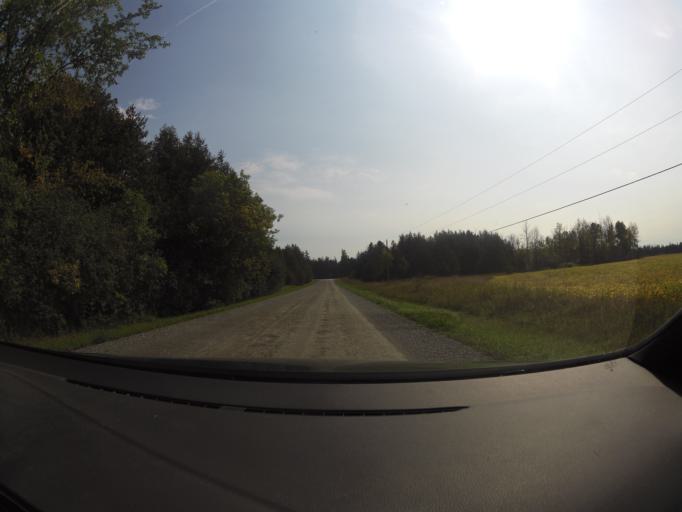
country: CA
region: Ontario
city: Carleton Place
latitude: 45.3269
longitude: -76.1763
